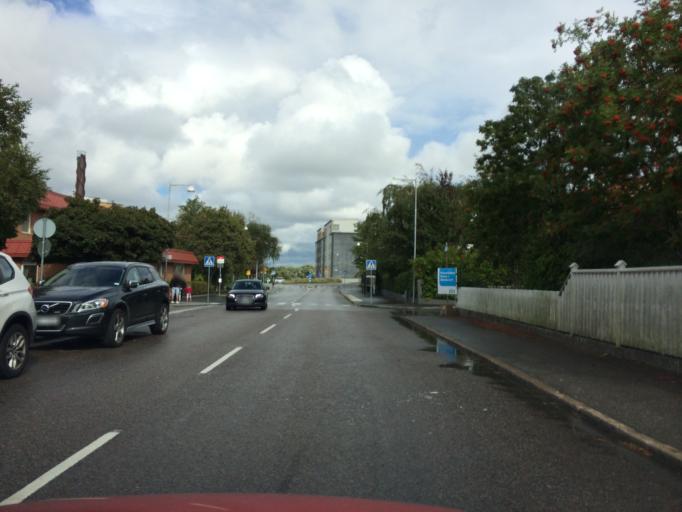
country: SE
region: Stockholm
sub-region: Stockholms Kommun
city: Bromma
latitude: 59.3036
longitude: 17.9753
